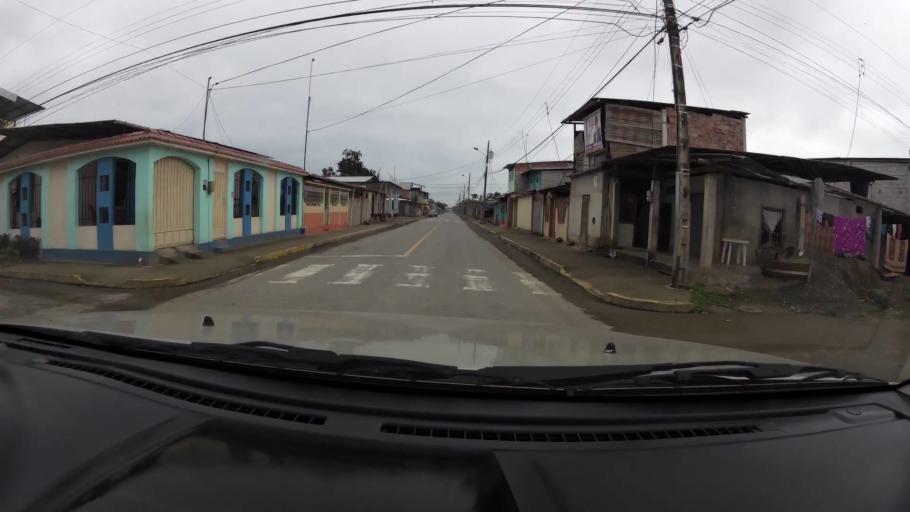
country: EC
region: El Oro
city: Pasaje
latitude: -3.3380
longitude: -79.8098
